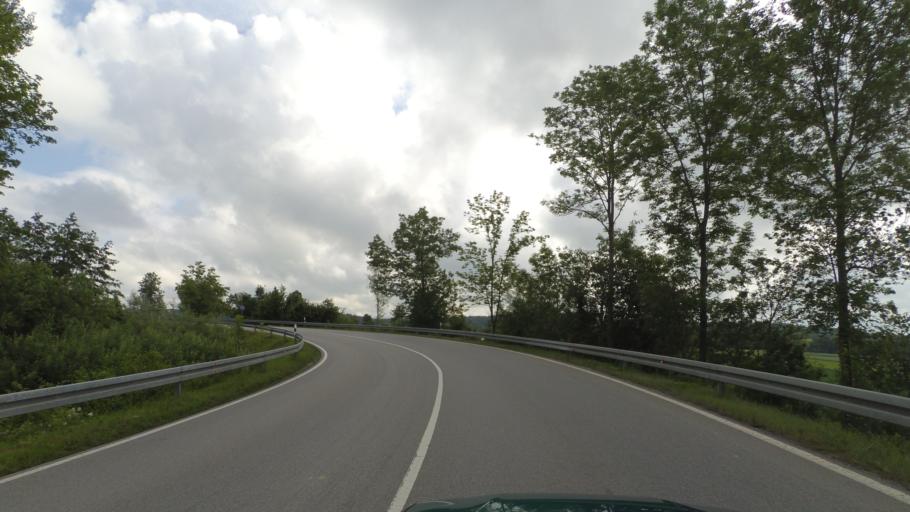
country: DE
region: Bavaria
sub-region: Lower Bavaria
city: Steinach
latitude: 48.9492
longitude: 12.6217
